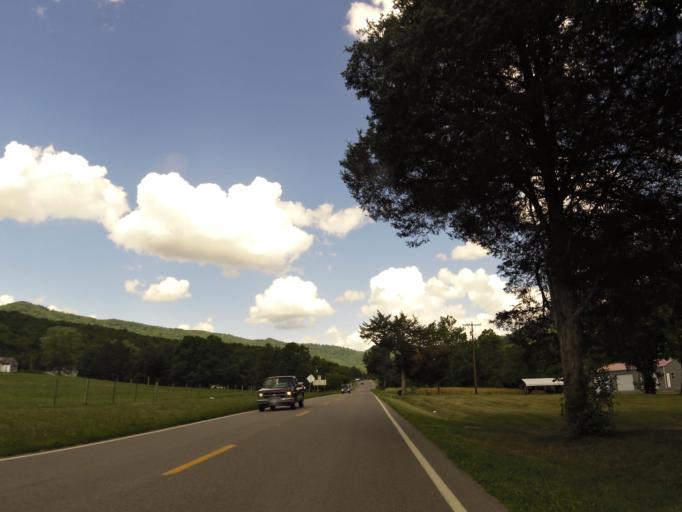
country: US
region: Virginia
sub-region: Lee County
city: Dryden
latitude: 36.7080
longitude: -82.9670
